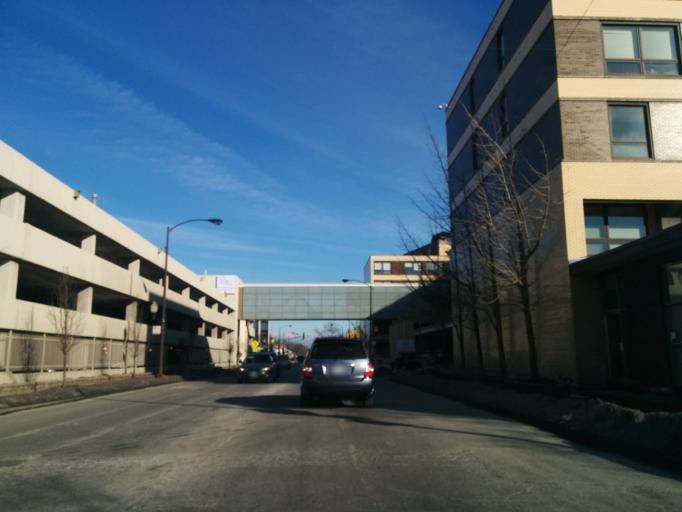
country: US
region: Illinois
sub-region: Cook County
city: Harwood Heights
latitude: 41.9459
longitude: -87.7688
